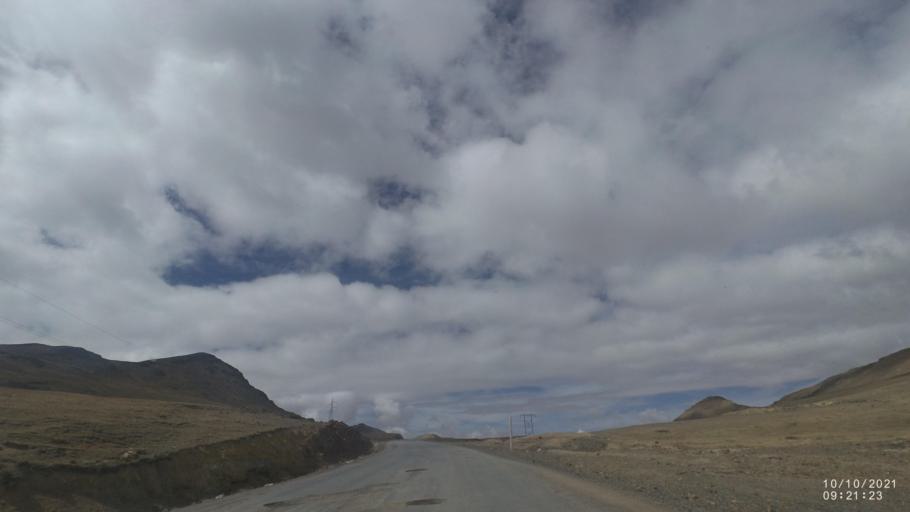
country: BO
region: La Paz
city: Quime
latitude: -17.0674
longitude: -67.2985
